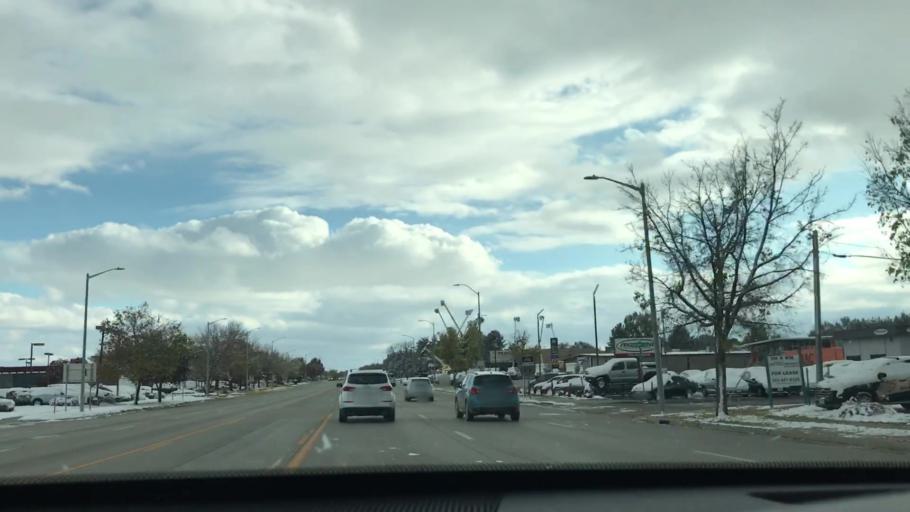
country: US
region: Colorado
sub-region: Boulder County
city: Longmont
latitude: 40.1509
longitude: -105.1034
